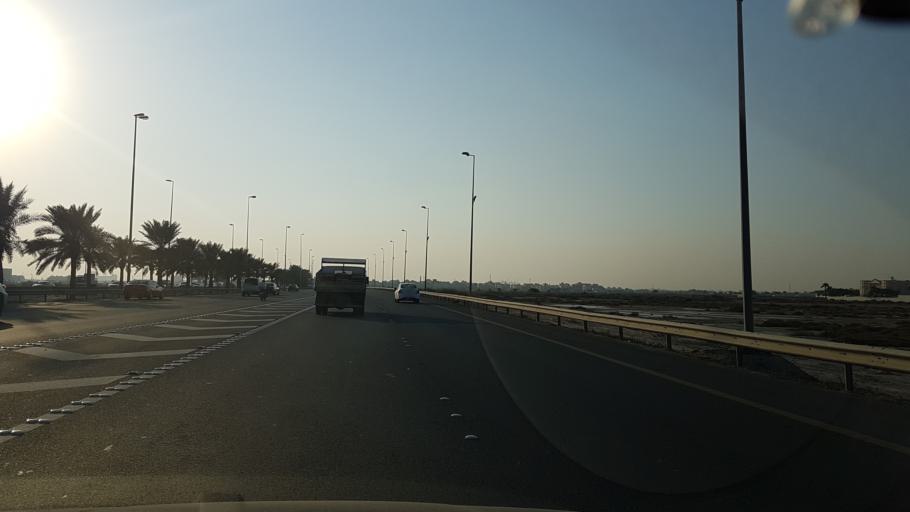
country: BH
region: Northern
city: Madinat `Isa
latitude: 26.1957
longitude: 50.5289
